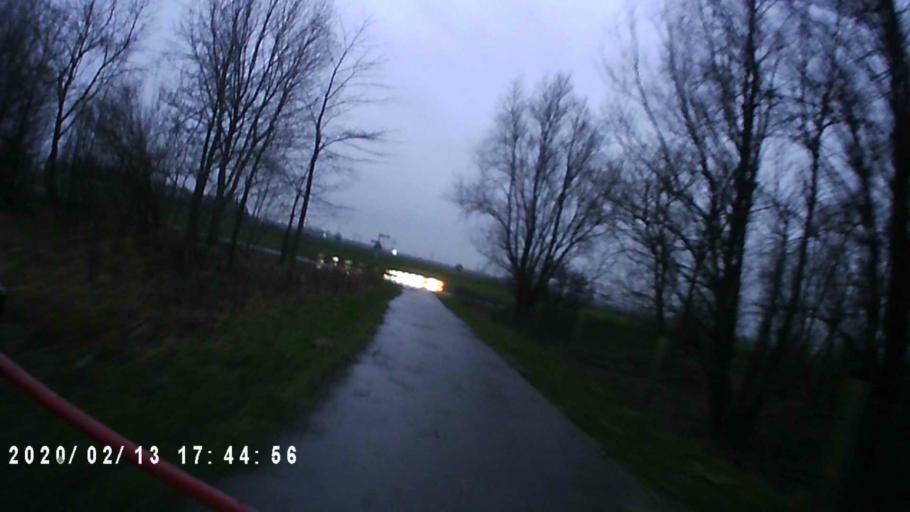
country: NL
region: Groningen
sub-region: Gemeente Zuidhorn
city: Aduard
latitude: 53.2297
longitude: 6.4797
